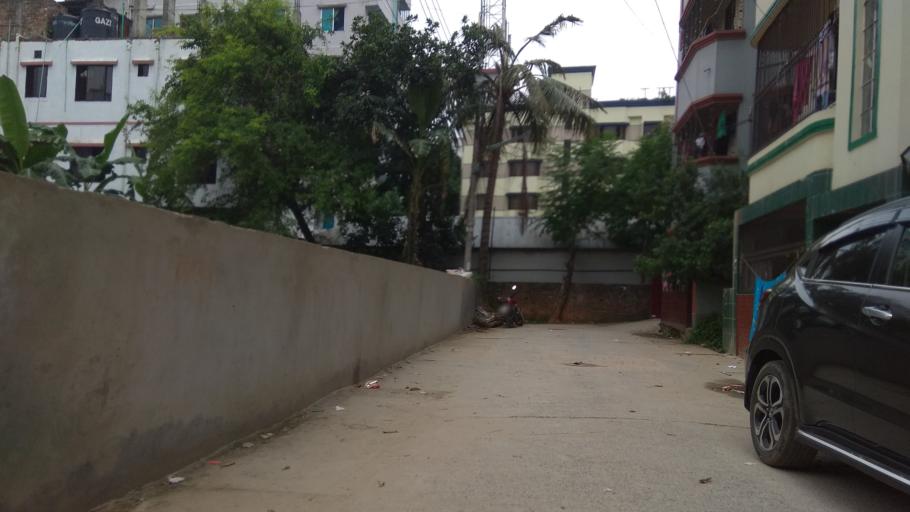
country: BD
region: Dhaka
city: Tungi
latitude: 23.8213
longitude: 90.3581
